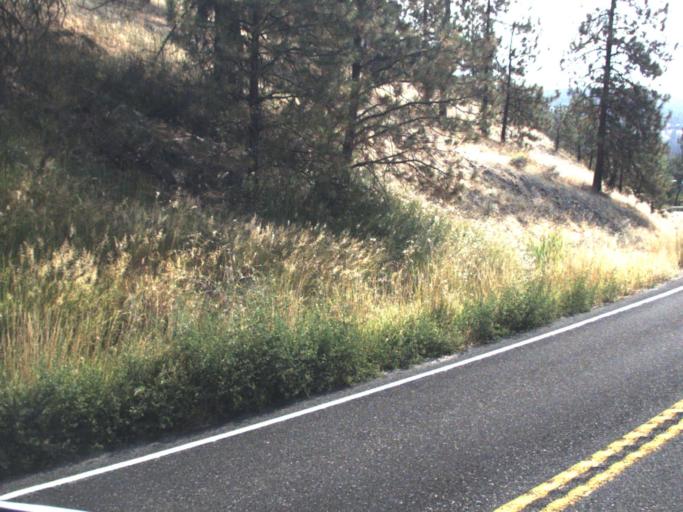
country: US
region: Washington
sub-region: Spokane County
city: Fairwood
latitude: 47.8045
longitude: -117.5538
